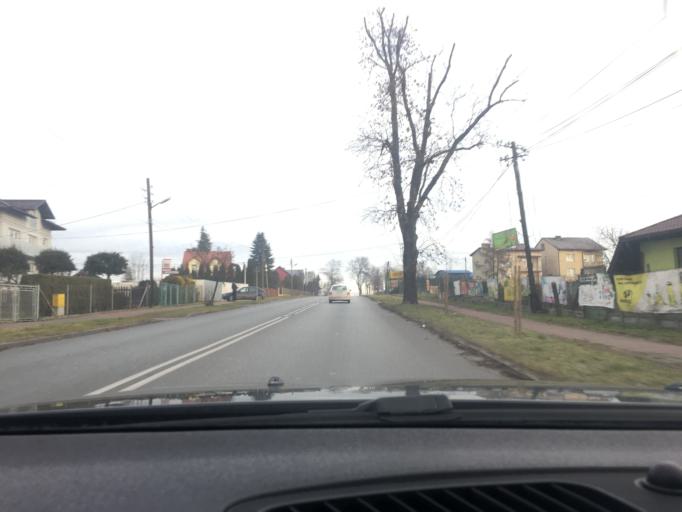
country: PL
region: Swietokrzyskie
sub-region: Powiat jedrzejowski
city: Jedrzejow
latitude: 50.6426
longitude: 20.3092
